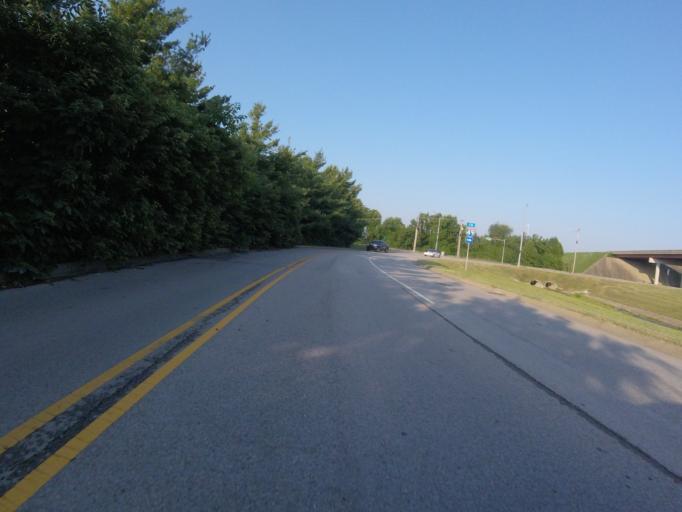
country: US
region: Arkansas
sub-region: Washington County
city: Johnson
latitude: 36.1110
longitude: -94.1626
